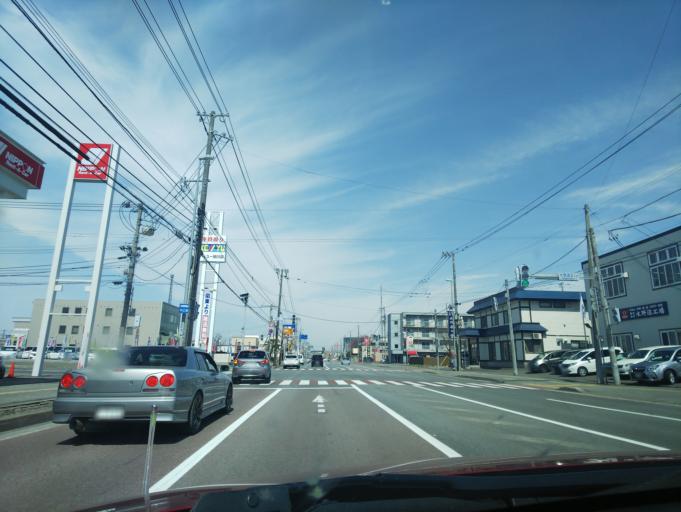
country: JP
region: Hokkaido
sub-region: Asahikawa-shi
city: Asahikawa
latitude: 43.7759
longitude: 142.3841
